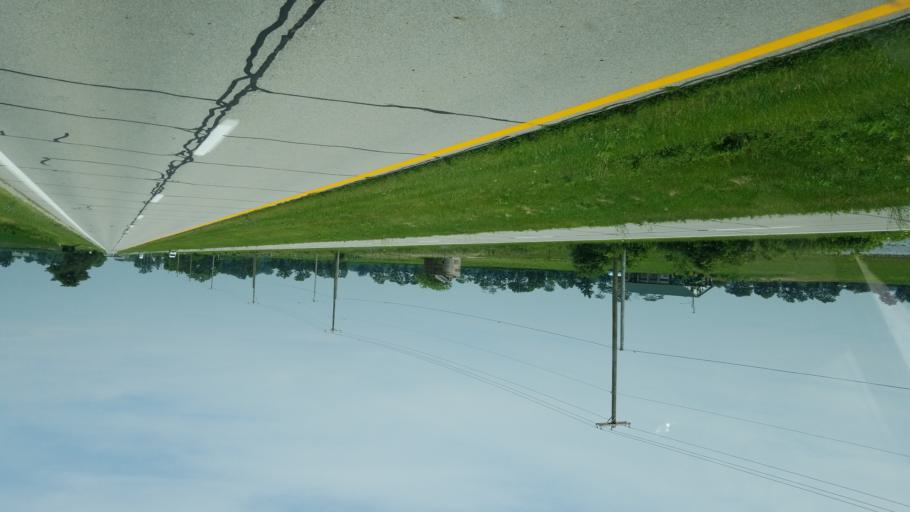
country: US
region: Ohio
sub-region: Madison County
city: London
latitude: 39.9391
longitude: -83.3784
